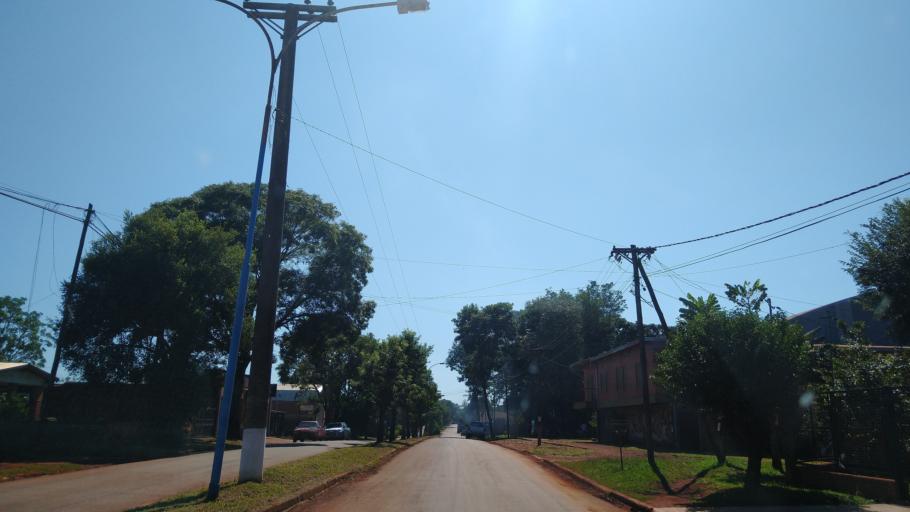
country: AR
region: Misiones
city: Puerto Libertad
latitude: -25.9771
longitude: -54.5715
